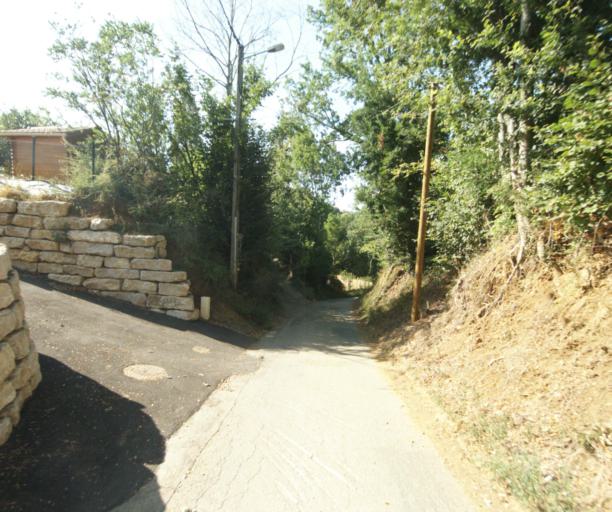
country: FR
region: Rhone-Alpes
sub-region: Departement du Rhone
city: Saint-Pierre-la-Palud
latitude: 45.7817
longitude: 4.6179
